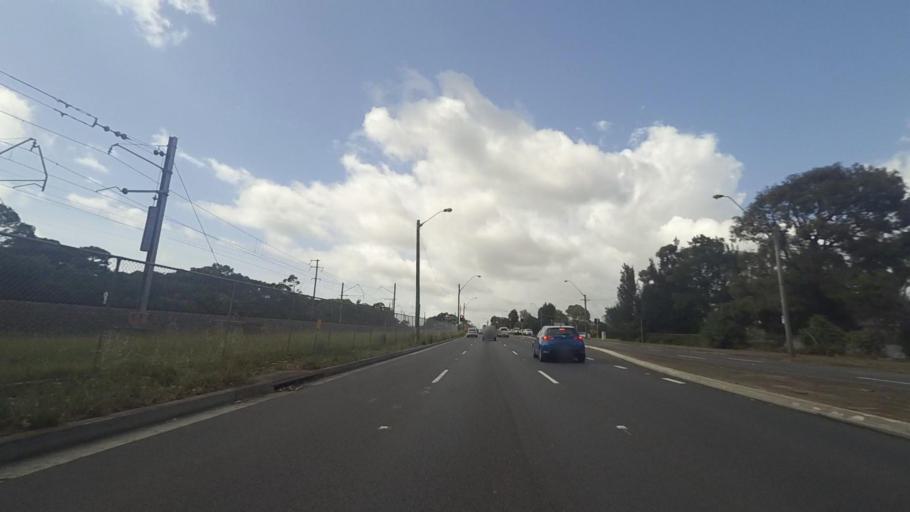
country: AU
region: New South Wales
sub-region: Sutherland Shire
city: Engadine
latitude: -34.0740
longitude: 151.0115
